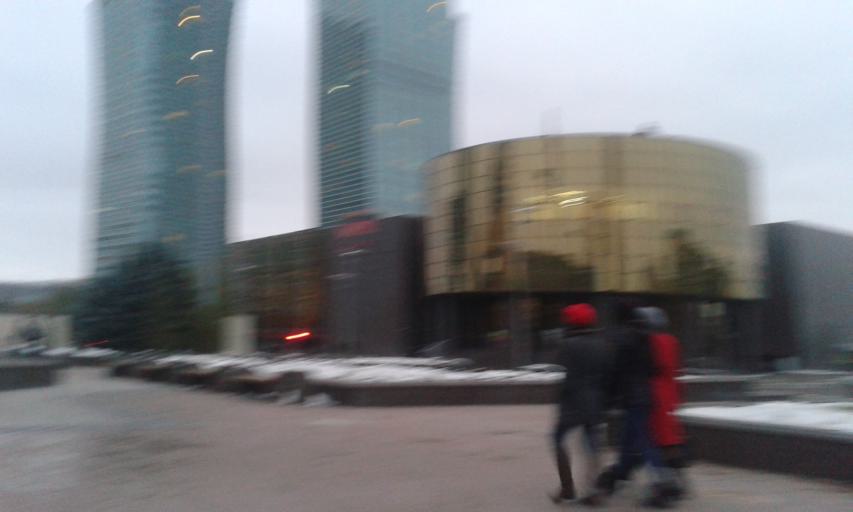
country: KZ
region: Astana Qalasy
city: Astana
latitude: 51.1299
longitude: 71.4195
